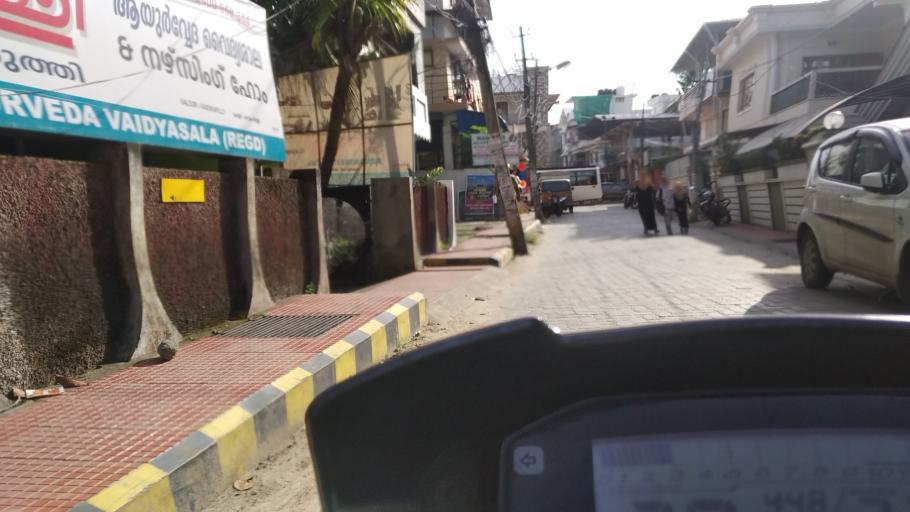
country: IN
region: Kerala
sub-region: Ernakulam
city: Elur
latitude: 10.0062
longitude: 76.2953
